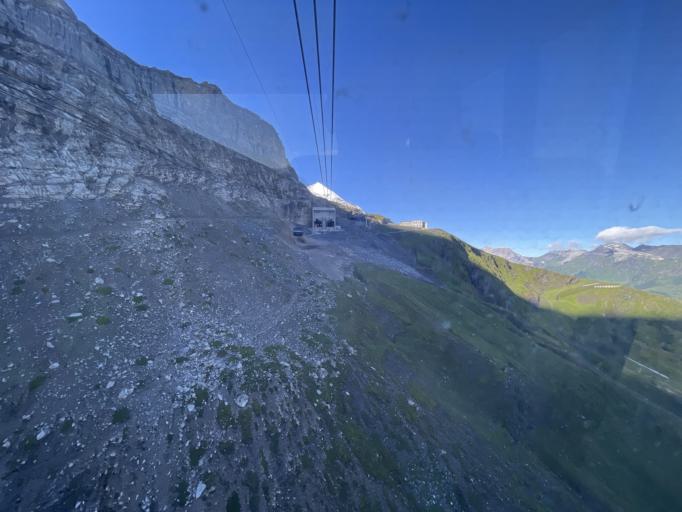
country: CH
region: Bern
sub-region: Interlaken-Oberhasli District
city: Lauterbrunnen
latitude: 46.5776
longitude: 7.9777
